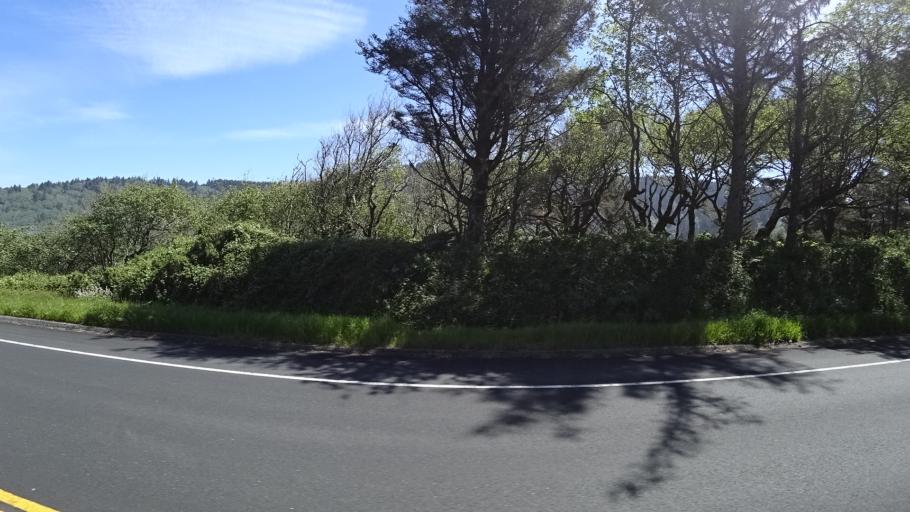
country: US
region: California
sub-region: Humboldt County
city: Westhaven-Moonstone
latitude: 41.2648
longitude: -124.0978
